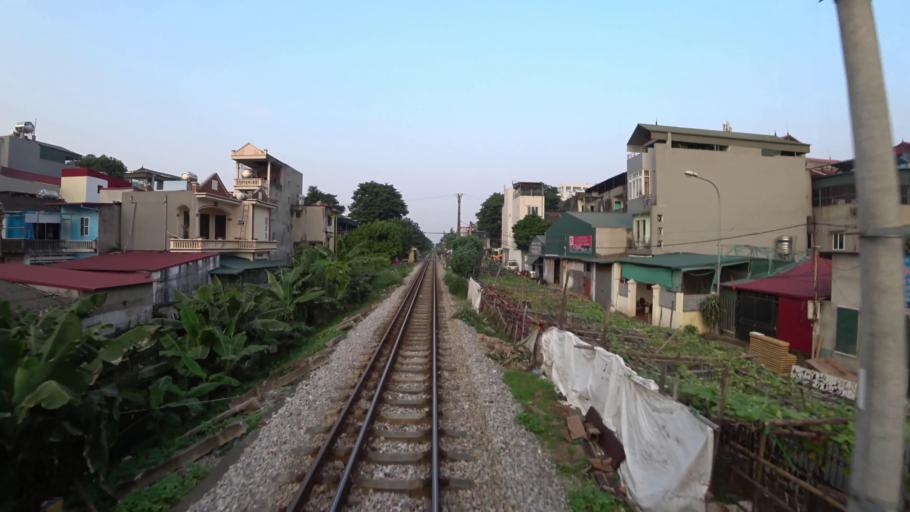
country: VN
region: Ha Noi
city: Trau Quy
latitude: 21.0807
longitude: 105.9115
